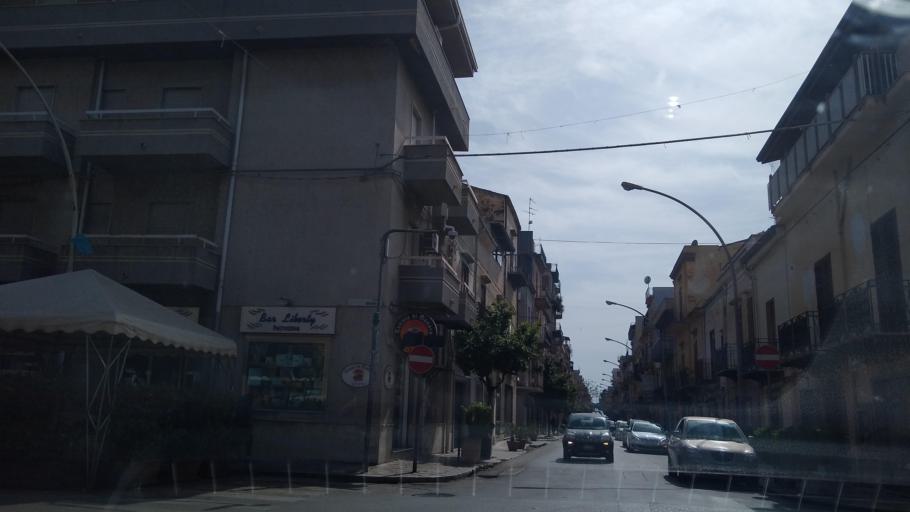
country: IT
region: Sicily
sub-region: Palermo
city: Partinico
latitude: 38.0450
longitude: 13.1158
